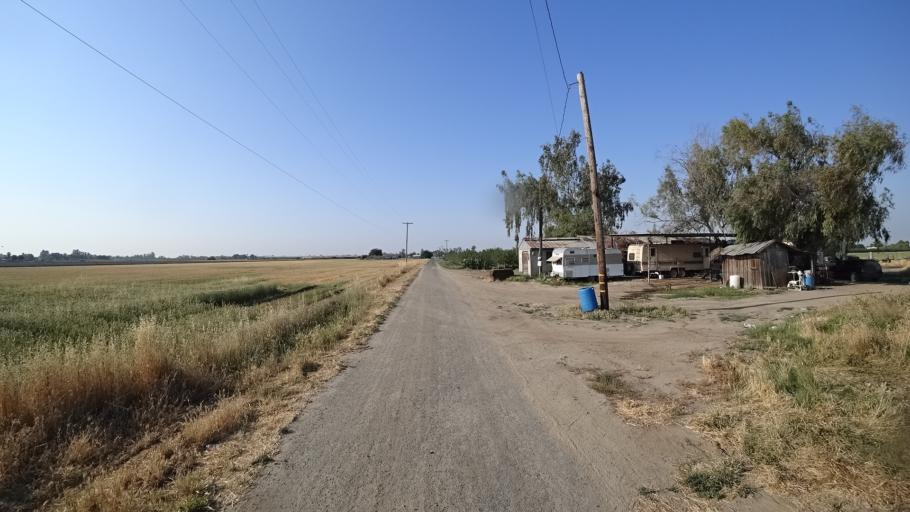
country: US
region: California
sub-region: Fresno County
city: Riverdale
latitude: 36.3837
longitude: -119.8433
